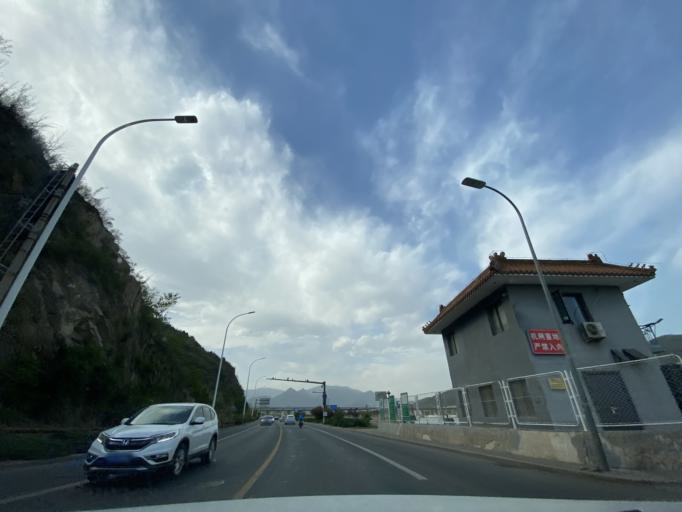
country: CN
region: Beijing
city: Chengzi
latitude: 39.9586
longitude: 116.0927
